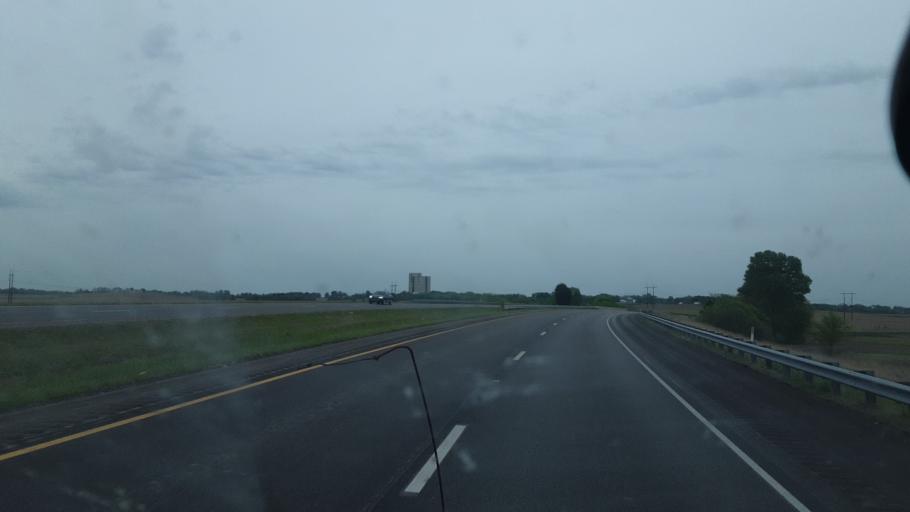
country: US
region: Indiana
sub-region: Posey County
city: Poseyville
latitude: 38.1824
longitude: -87.7662
